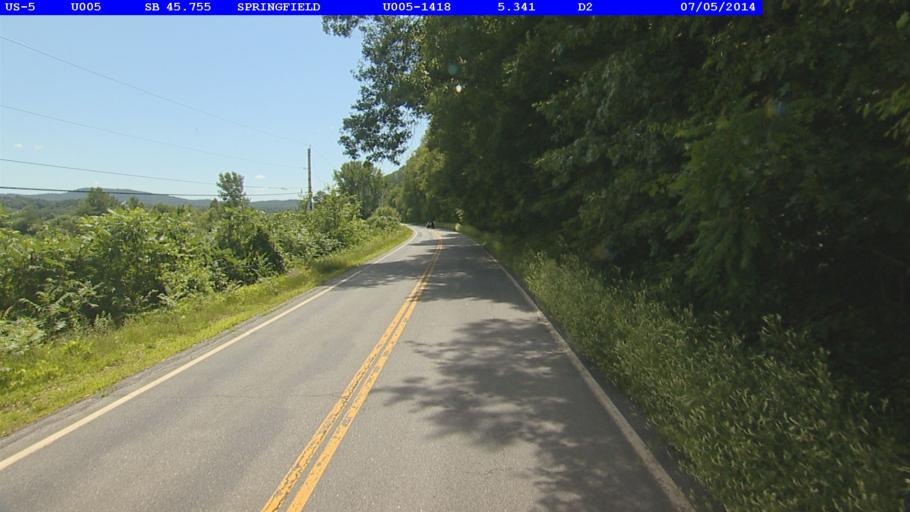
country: US
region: New Hampshire
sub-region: Sullivan County
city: Charlestown
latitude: 43.2906
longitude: -72.4130
